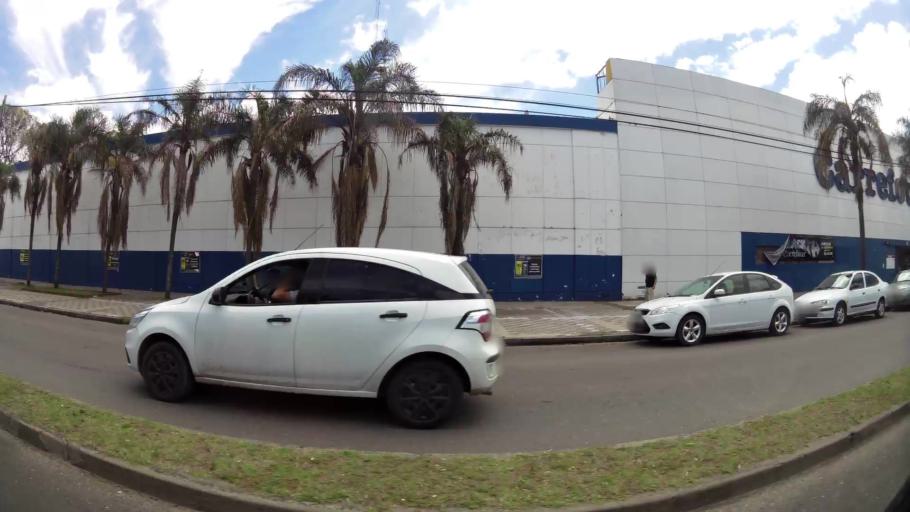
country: AR
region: Santa Fe
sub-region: Departamento de Rosario
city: Rosario
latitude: -32.9702
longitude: -60.6288
